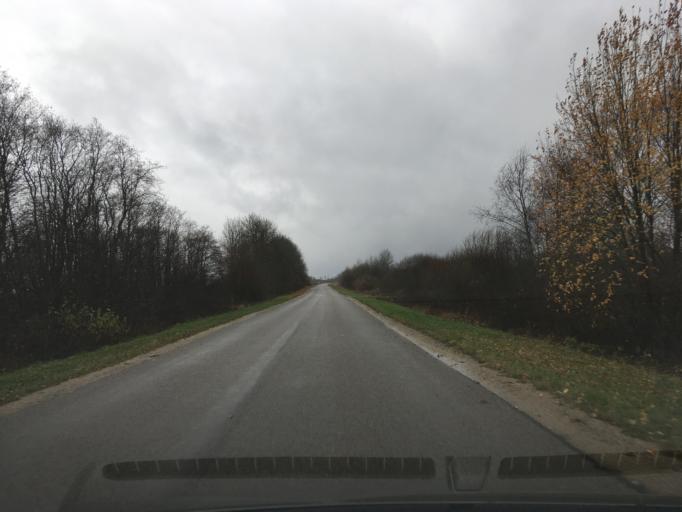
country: EE
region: Laeaene
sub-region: Lihula vald
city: Lihula
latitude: 58.6996
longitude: 23.8555
